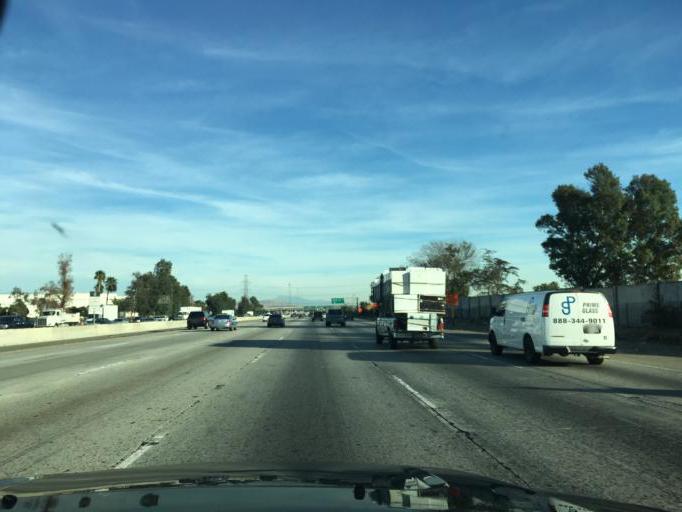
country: US
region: California
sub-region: Riverside County
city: Mira Loma
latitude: 34.0271
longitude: -117.5695
